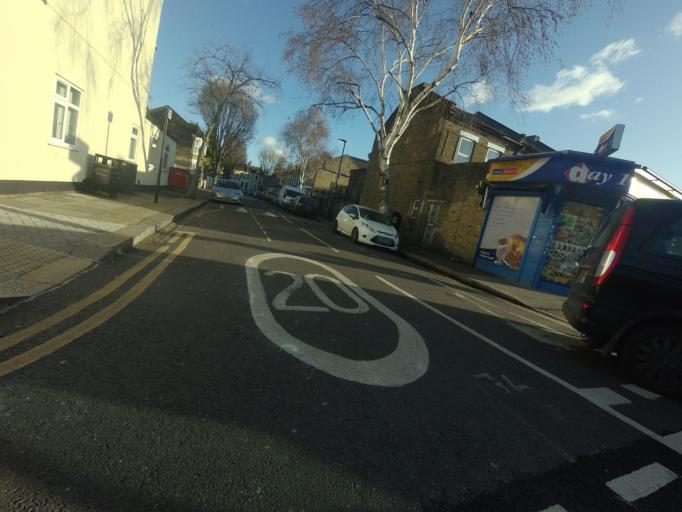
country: GB
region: England
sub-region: Greater London
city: East Ham
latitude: 51.5528
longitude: 0.0254
